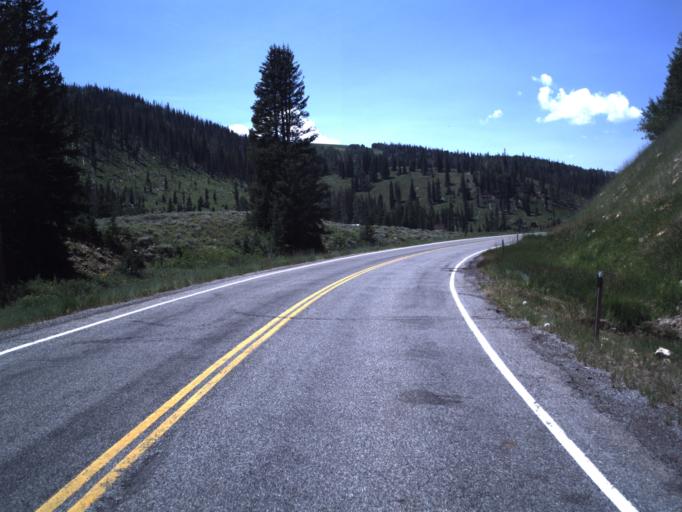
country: US
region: Utah
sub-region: Sanpete County
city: Fairview
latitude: 39.6479
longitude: -111.2578
